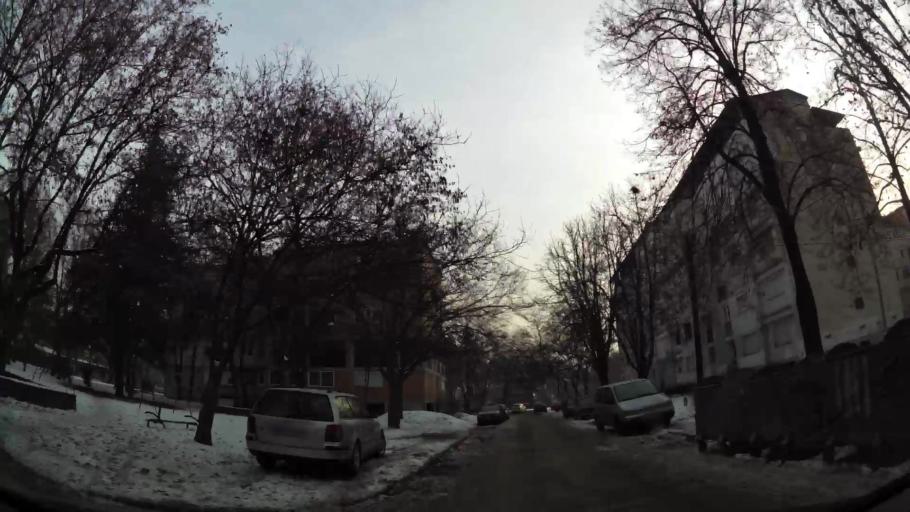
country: MK
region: Cair
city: Cair
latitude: 42.0195
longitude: 21.4469
